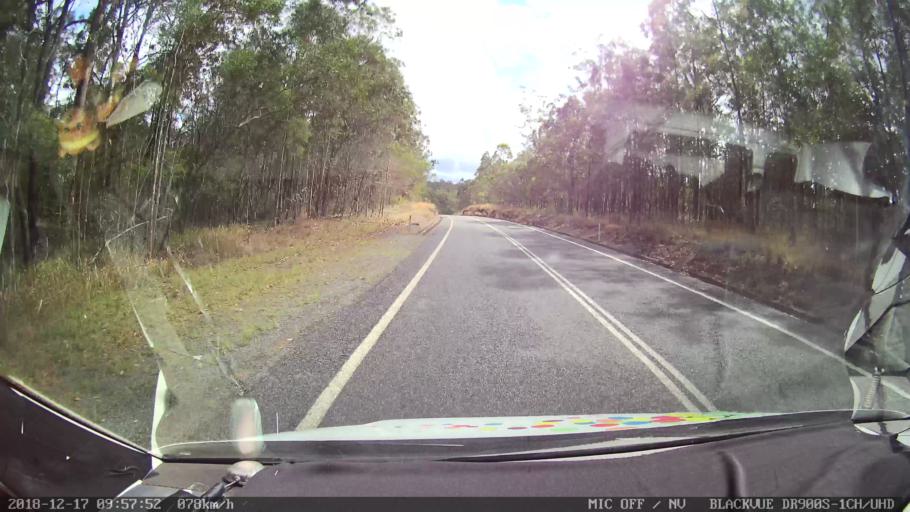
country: AU
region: New South Wales
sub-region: Tenterfield Municipality
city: Carrolls Creek
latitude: -28.9235
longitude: 152.4026
